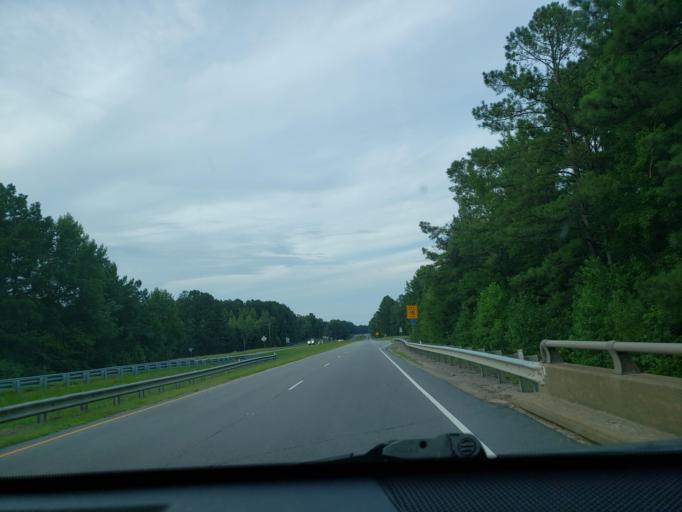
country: US
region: Virginia
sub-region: Brunswick County
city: Lawrenceville
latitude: 36.7668
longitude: -77.8244
